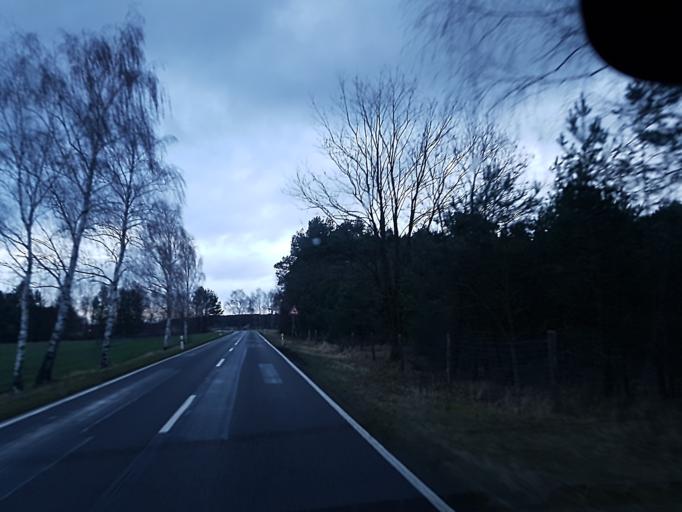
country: DE
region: Brandenburg
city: Finsterwalde
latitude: 51.5565
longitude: 13.6730
